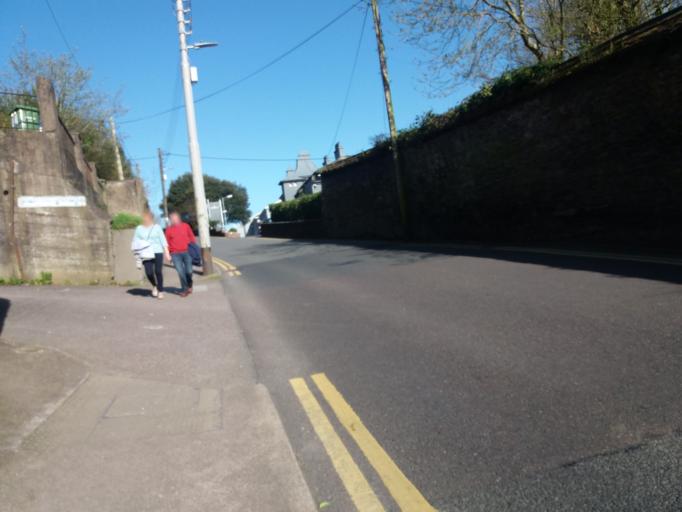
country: IE
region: Munster
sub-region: County Cork
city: Cork
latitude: 51.9048
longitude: -8.4533
